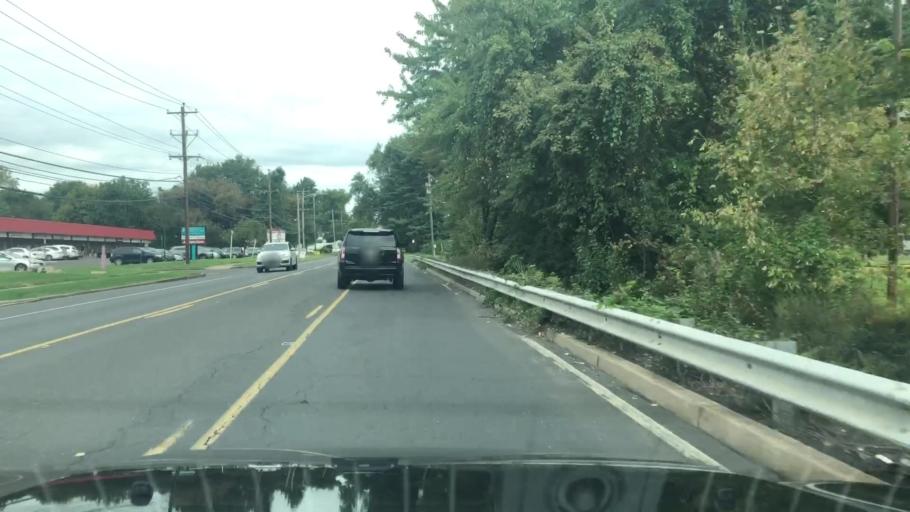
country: US
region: Pennsylvania
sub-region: Bucks County
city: Fairless Hills
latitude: 40.1685
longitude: -74.8773
